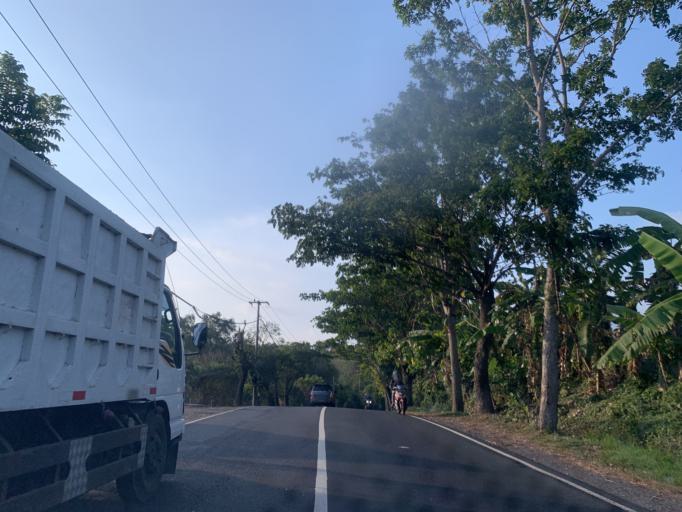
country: ID
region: Bali
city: Banjar Delodrurung
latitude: -8.5028
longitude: 114.9723
